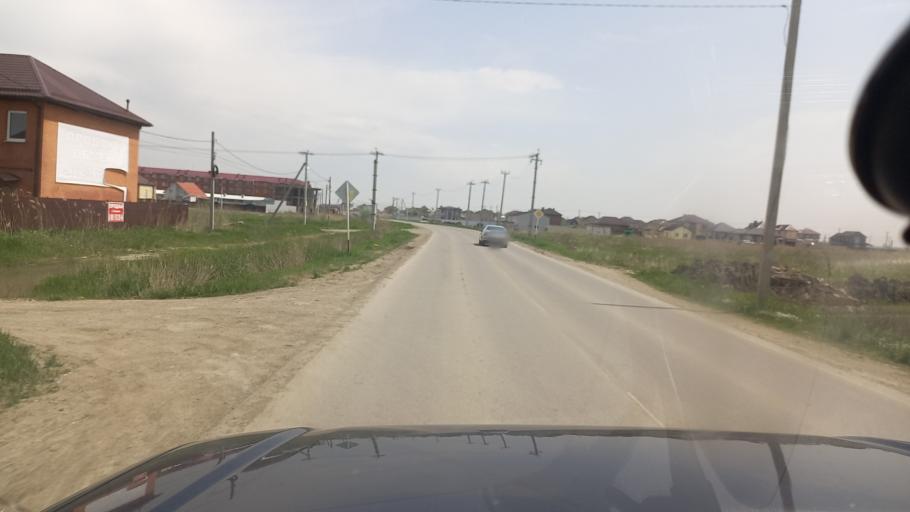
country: RU
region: Adygeya
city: Yablonovskiy
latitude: 44.9853
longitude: 38.9702
